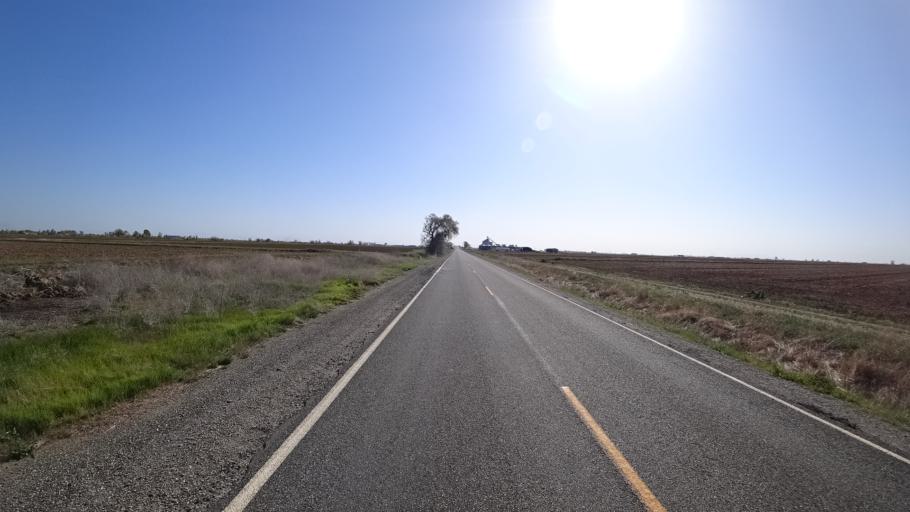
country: US
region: California
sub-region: Glenn County
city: Willows
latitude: 39.4950
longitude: -122.2085
